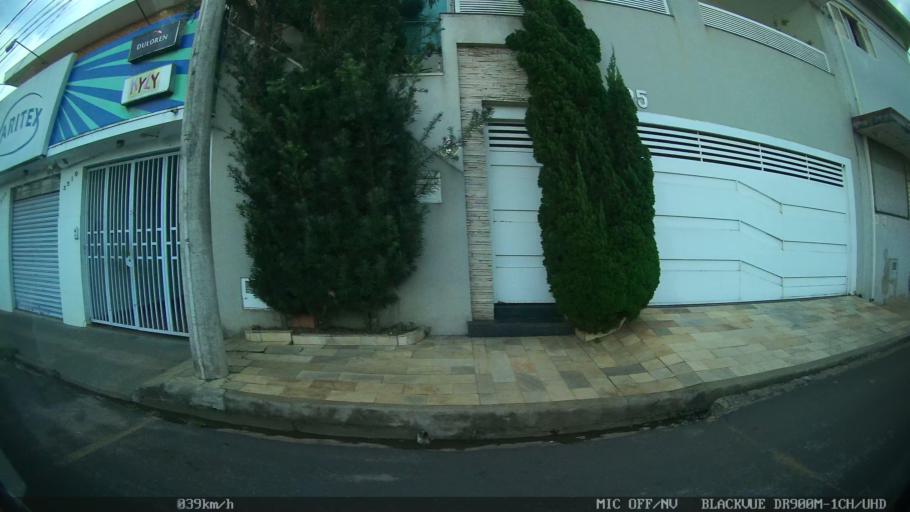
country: BR
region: Sao Paulo
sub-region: Franca
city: Franca
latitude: -20.5229
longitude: -47.4071
